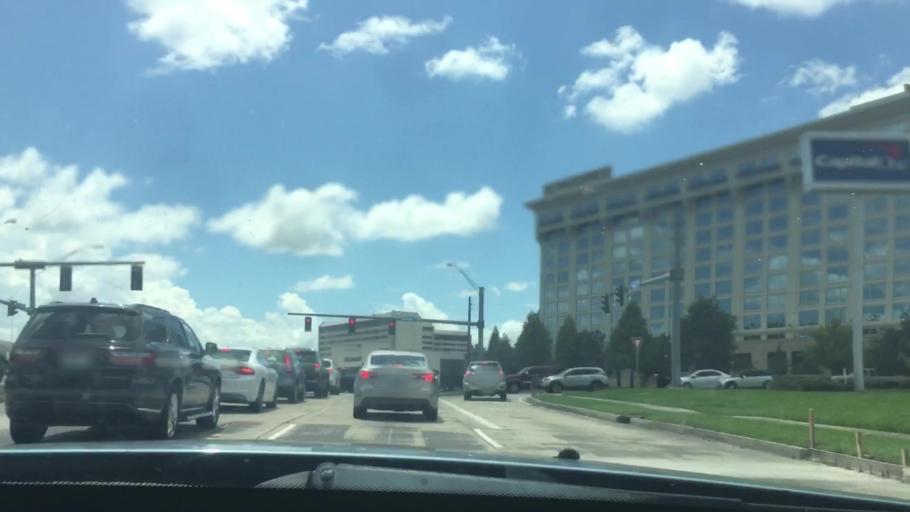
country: US
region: Louisiana
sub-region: East Baton Rouge Parish
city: Inniswold
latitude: 30.3898
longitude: -91.0924
